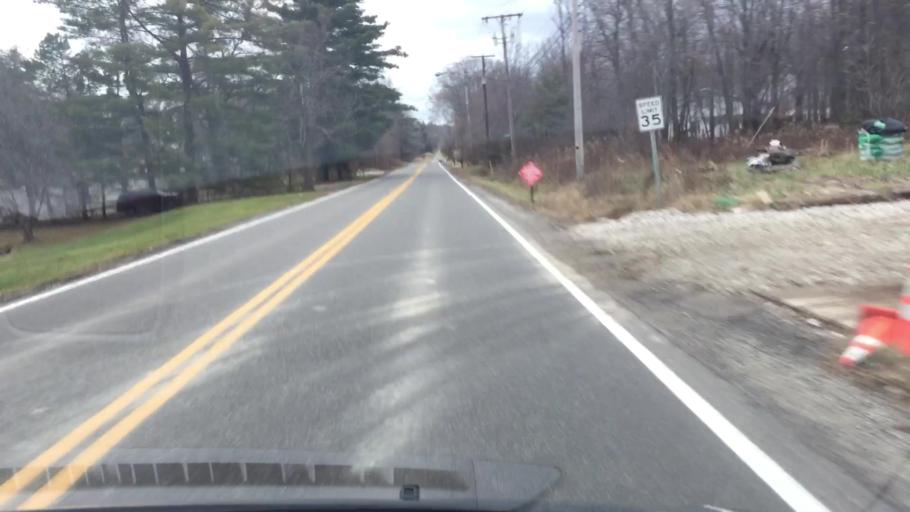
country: US
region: Ohio
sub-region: Summit County
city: Boston Heights
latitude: 41.2335
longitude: -81.4945
